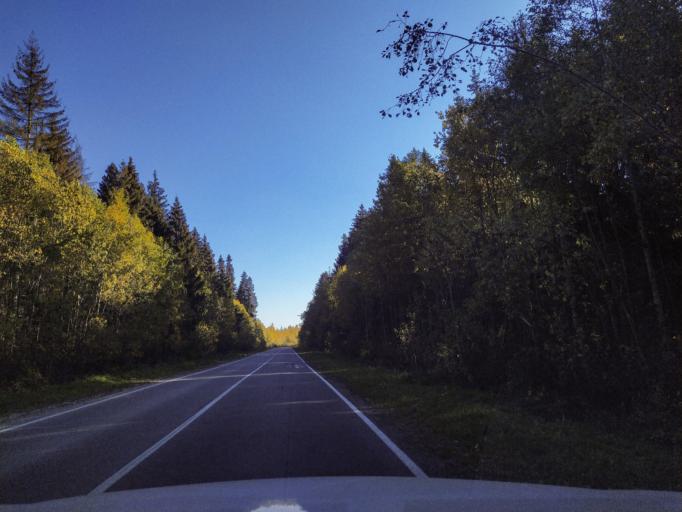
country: RU
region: Leningrad
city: Siverskiy
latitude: 59.3058
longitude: 30.0321
